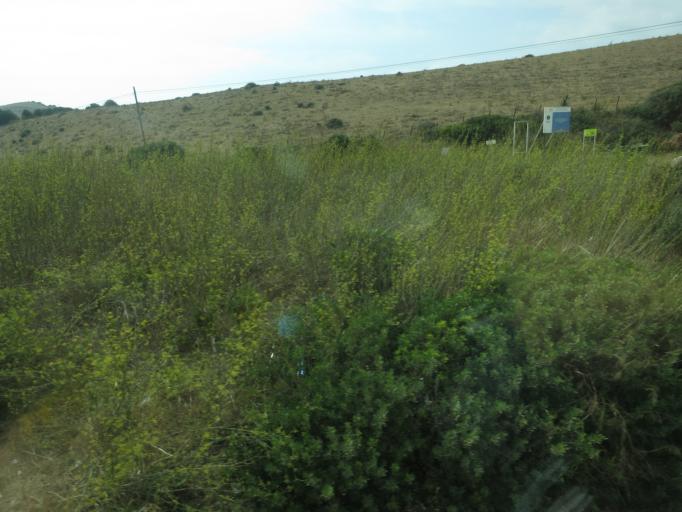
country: ES
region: Andalusia
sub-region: Provincia de Cadiz
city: Tarifa
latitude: 36.0246
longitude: -5.5921
